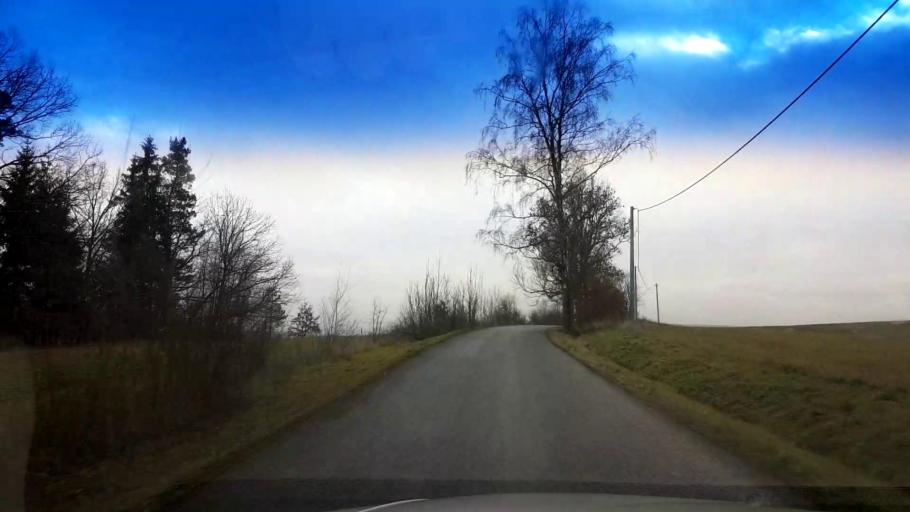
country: CZ
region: Karlovarsky
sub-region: Okres Cheb
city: Cheb
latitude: 50.0435
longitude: 12.3716
